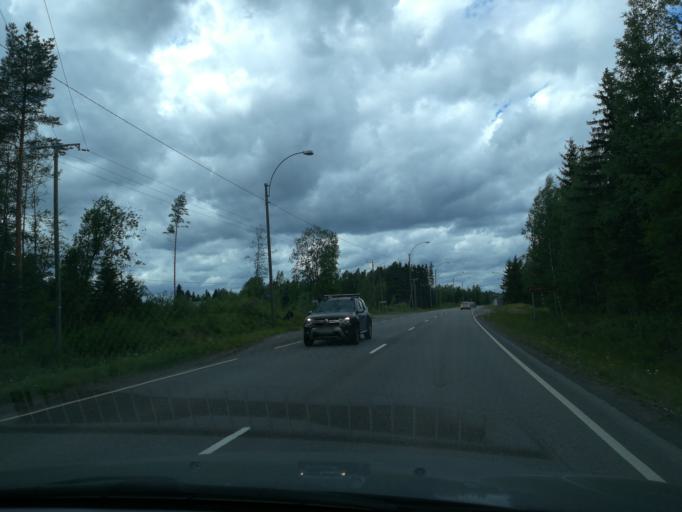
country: FI
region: South Karelia
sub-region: Lappeenranta
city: Lappeenranta
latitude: 61.0523
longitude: 28.3268
